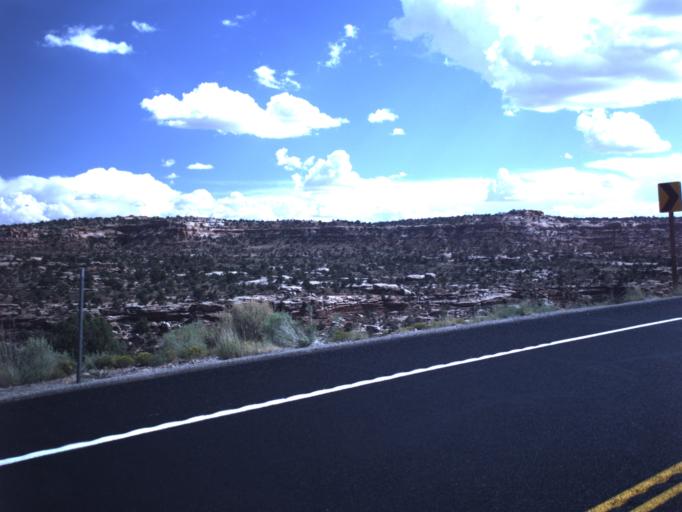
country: US
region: Utah
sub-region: Grand County
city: Moab
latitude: 38.6452
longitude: -109.7290
